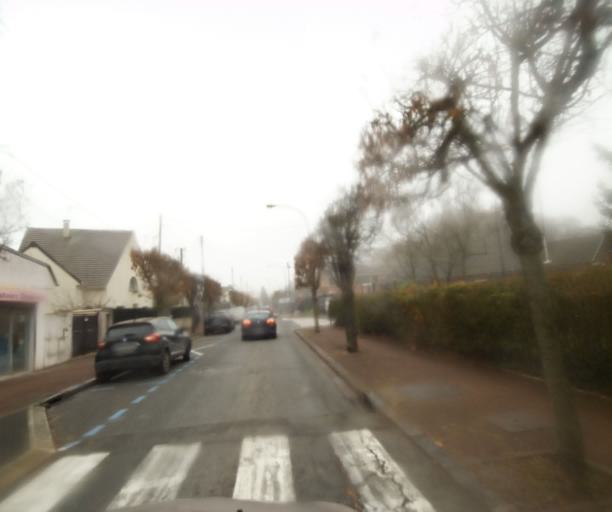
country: FR
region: Ile-de-France
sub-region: Departement de Seine-Saint-Denis
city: Vaujours
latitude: 48.9388
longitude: 2.5689
